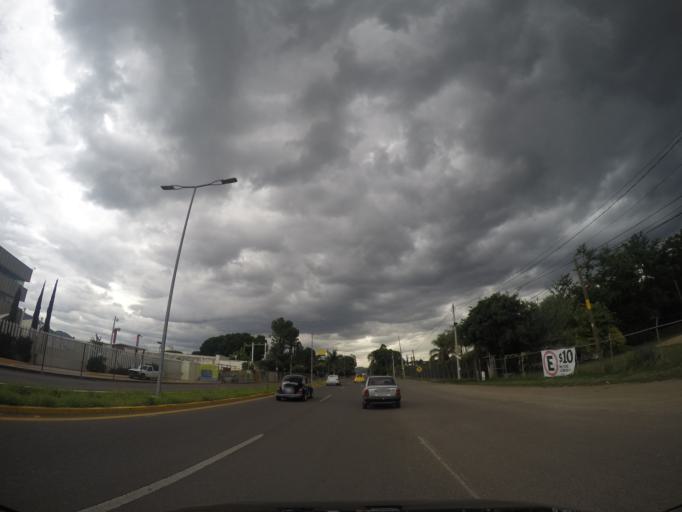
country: MX
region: Oaxaca
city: Tlalixtac de Cabrera
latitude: 17.0560
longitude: -96.6544
